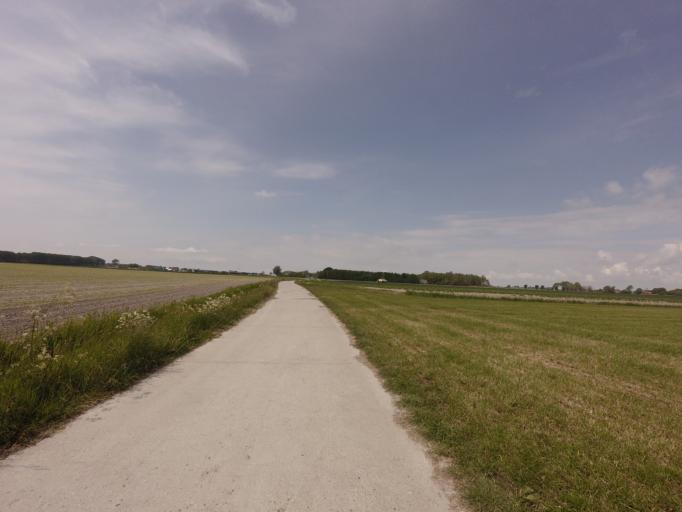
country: NL
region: Friesland
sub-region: Sudwest Fryslan
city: Bolsward
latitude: 53.1066
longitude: 5.4877
